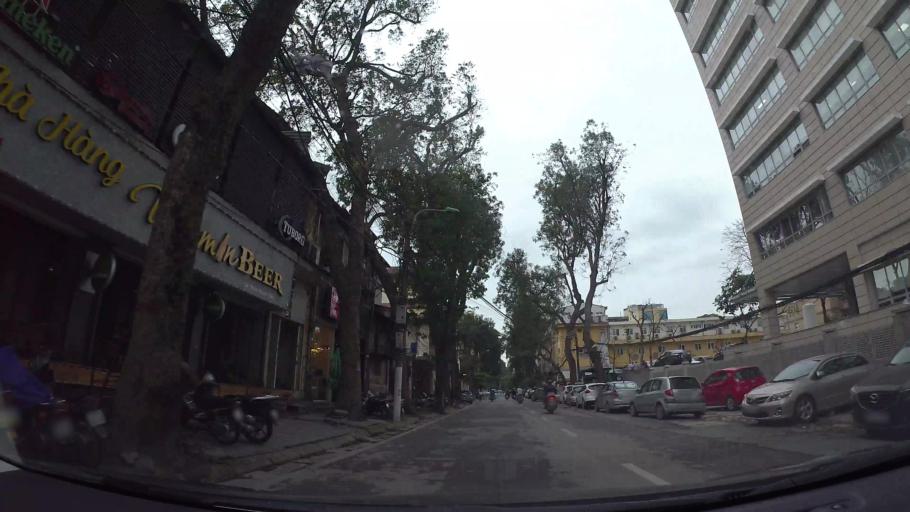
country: VN
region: Ha Noi
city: Hai BaTrung
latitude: 21.0168
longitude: 105.8593
